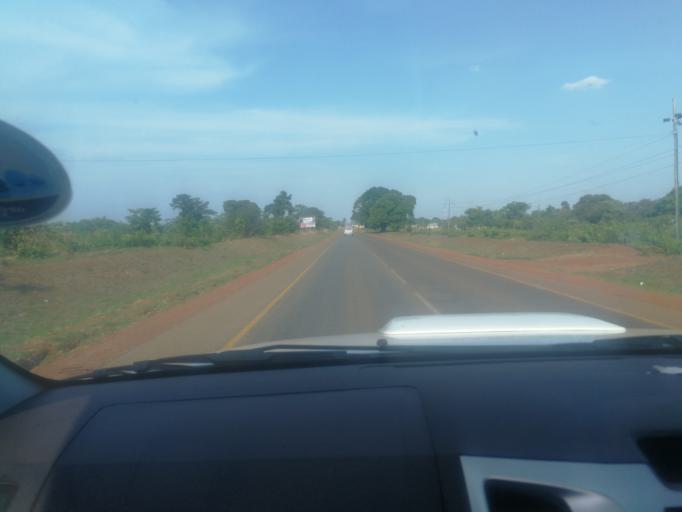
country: ZM
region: Northern
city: Kasama
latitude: -10.2176
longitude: 31.1439
